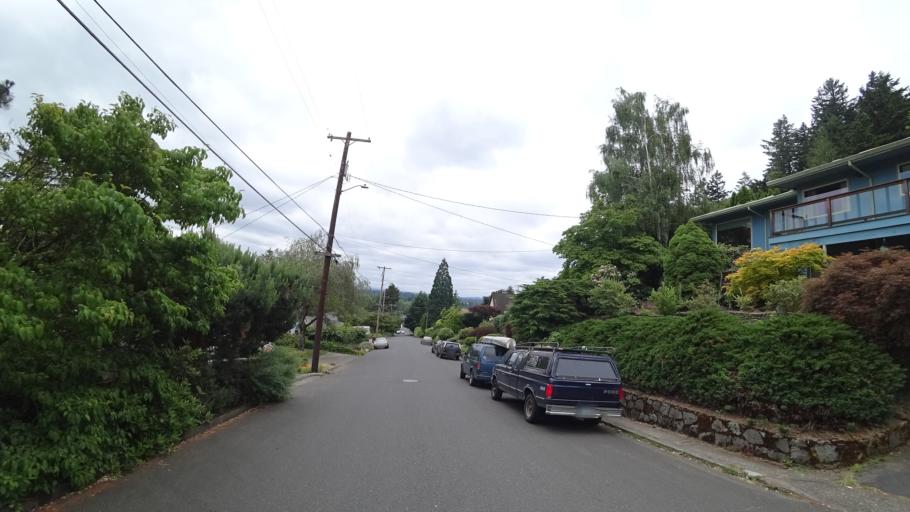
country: US
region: Oregon
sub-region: Multnomah County
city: Lents
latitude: 45.5112
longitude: -122.5890
